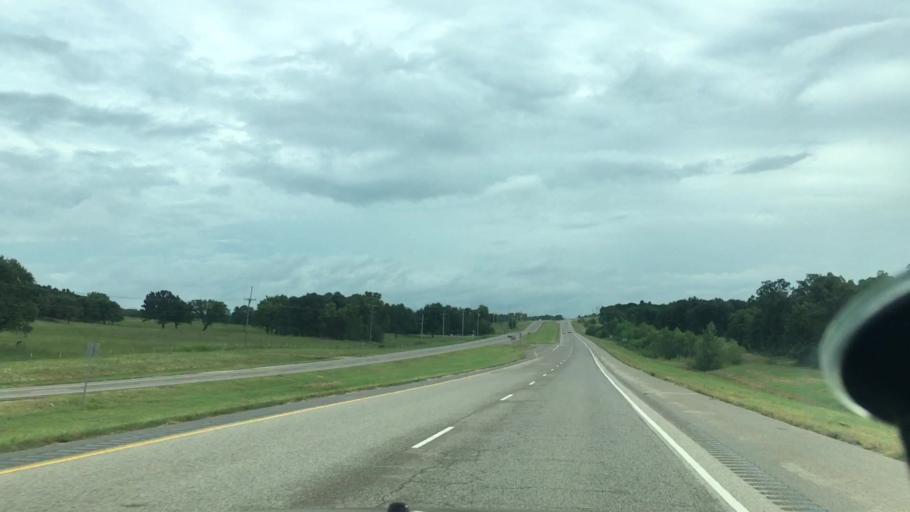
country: US
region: Oklahoma
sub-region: Seminole County
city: Seminole
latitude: 35.3431
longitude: -96.6719
